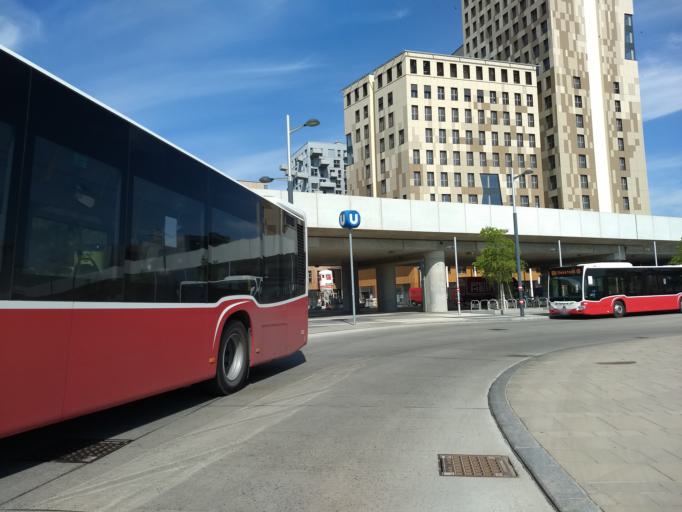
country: AT
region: Lower Austria
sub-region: Politischer Bezirk Ganserndorf
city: Gross-Enzersdorf
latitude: 48.2248
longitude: 16.5083
